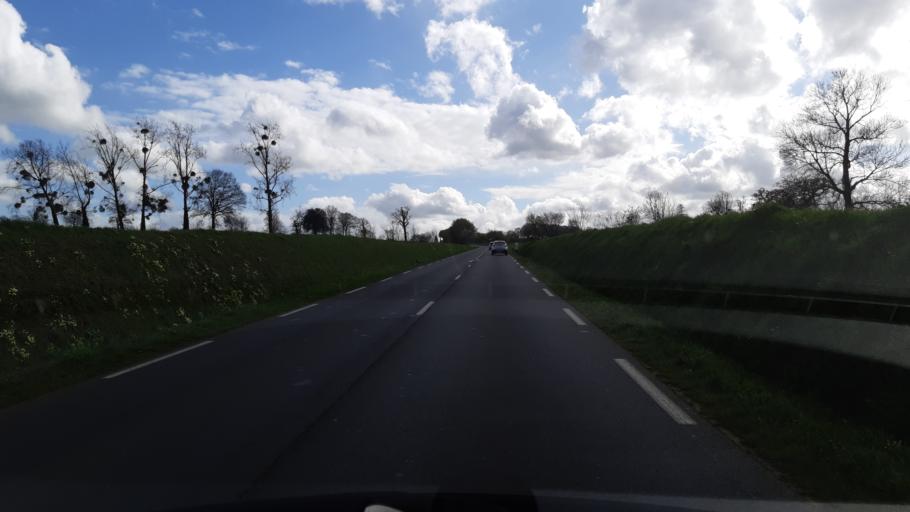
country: FR
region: Lower Normandy
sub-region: Departement de la Manche
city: Agneaux
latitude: 49.0358
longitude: -1.1337
